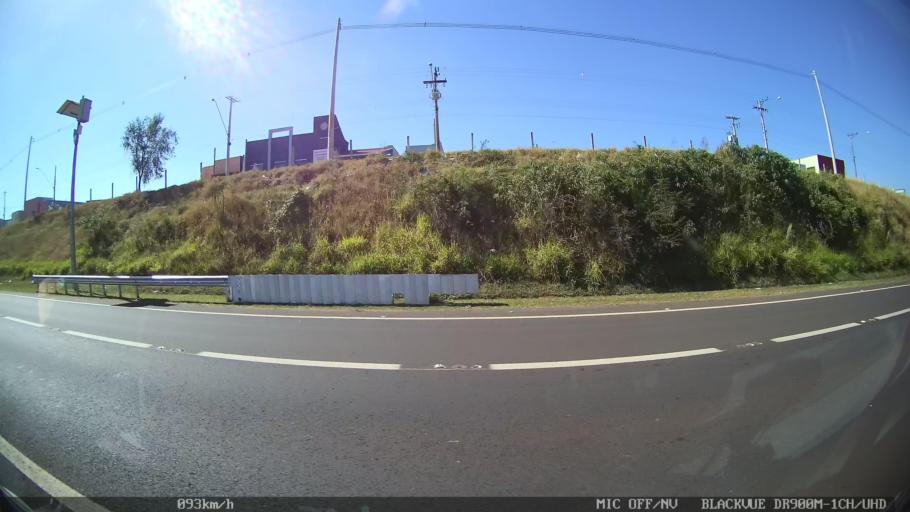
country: BR
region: Sao Paulo
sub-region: Franca
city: Franca
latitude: -20.4836
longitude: -47.4097
